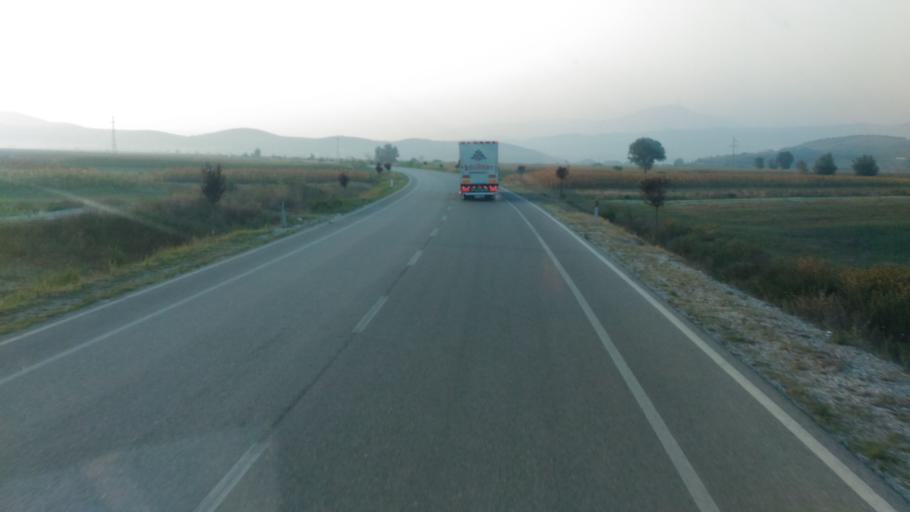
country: AL
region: Fier
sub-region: Rrethi i Fierit
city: Cakran
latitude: 40.5734
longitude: 19.6236
